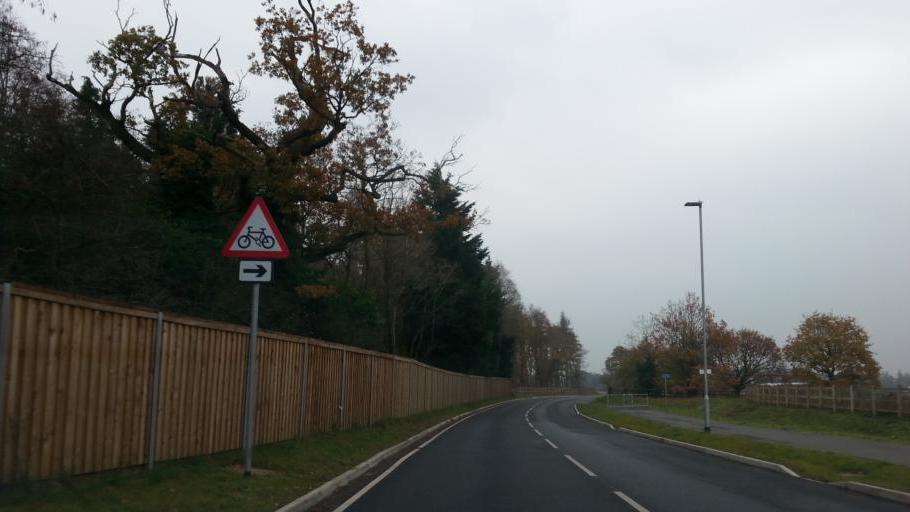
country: GB
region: England
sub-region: Suffolk
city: Thurston
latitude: 52.2452
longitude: 0.7803
